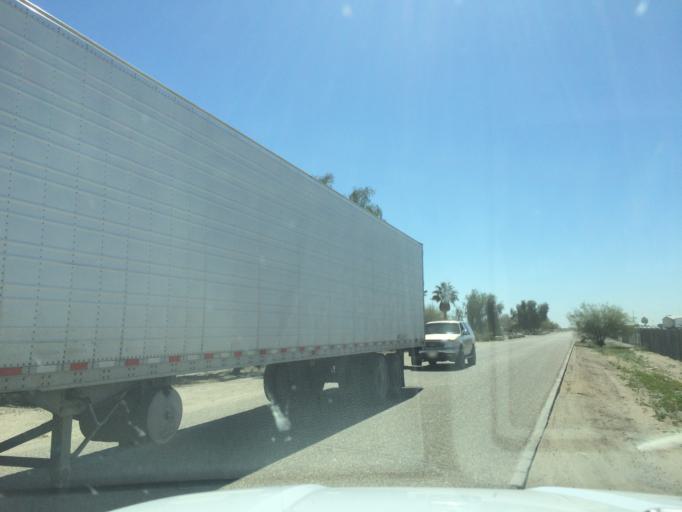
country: US
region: Arizona
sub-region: Yuma County
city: Yuma
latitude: 32.6550
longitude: -114.5770
